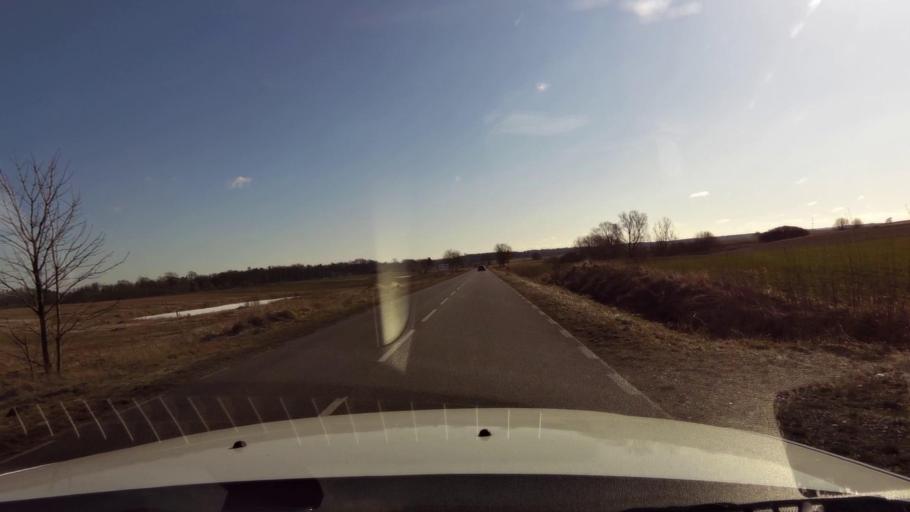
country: PL
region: West Pomeranian Voivodeship
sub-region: Powiat mysliborski
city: Nowogrodek Pomorski
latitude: 52.9875
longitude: 15.1075
